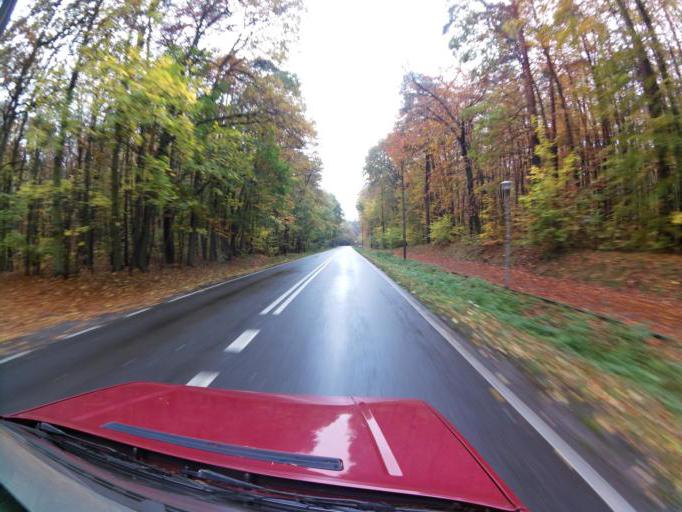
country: PL
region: West Pomeranian Voivodeship
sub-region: Szczecin
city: Szczecin
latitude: 53.4807
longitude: 14.4845
